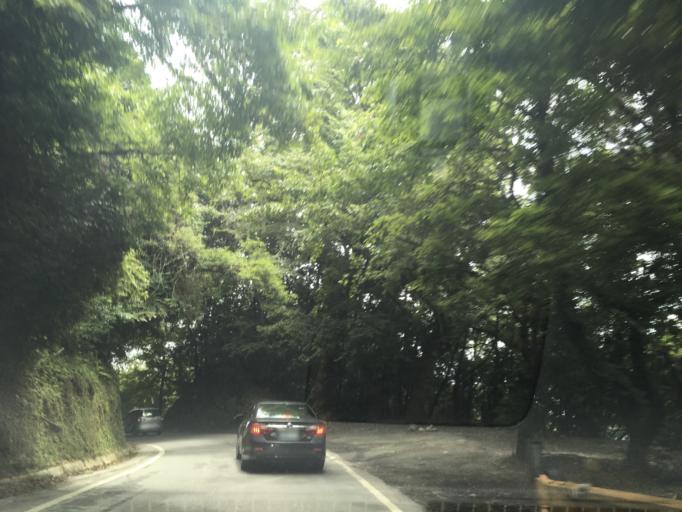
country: TW
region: Taiwan
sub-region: Hualien
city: Hualian
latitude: 24.1750
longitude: 121.3838
